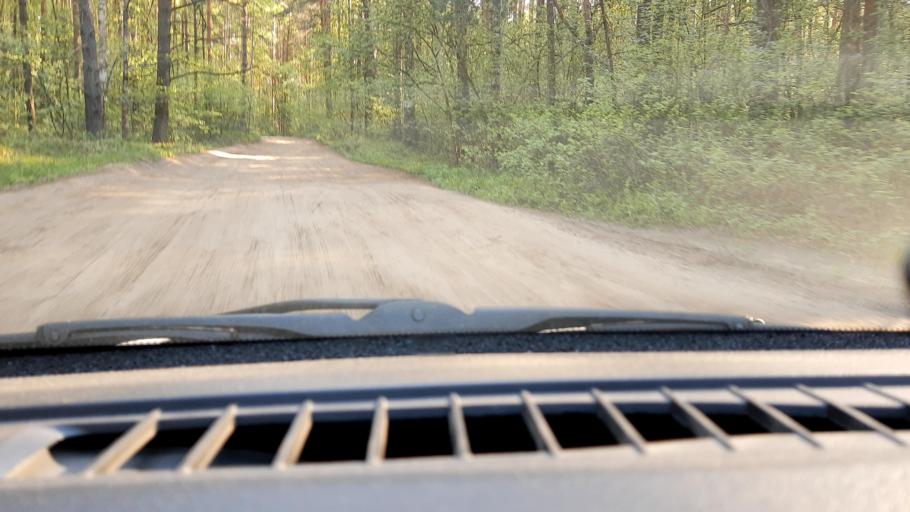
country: RU
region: Nizjnij Novgorod
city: Sitniki
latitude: 56.4168
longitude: 44.0649
